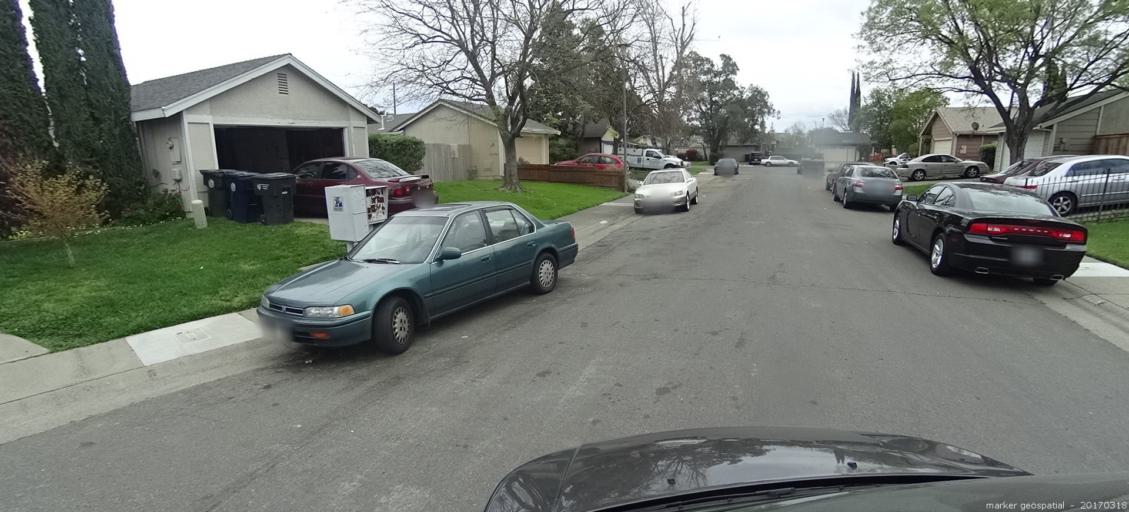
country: US
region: California
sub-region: Sacramento County
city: Parkway
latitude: 38.4813
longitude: -121.4586
